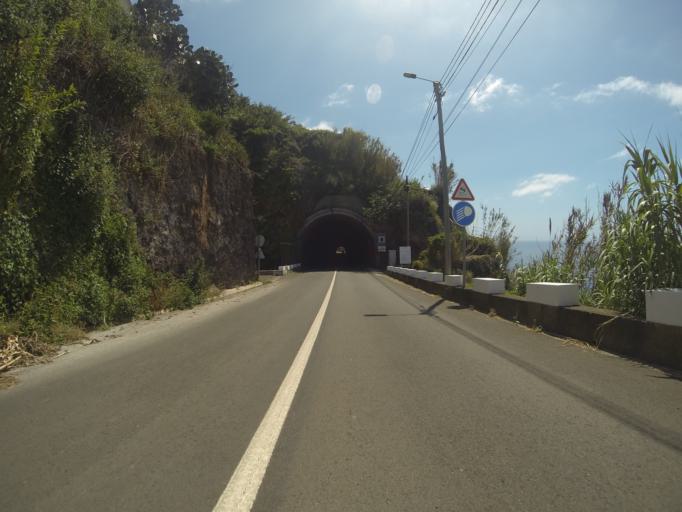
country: PT
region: Madeira
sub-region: Calheta
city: Arco da Calheta
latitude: 32.7073
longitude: -17.1453
